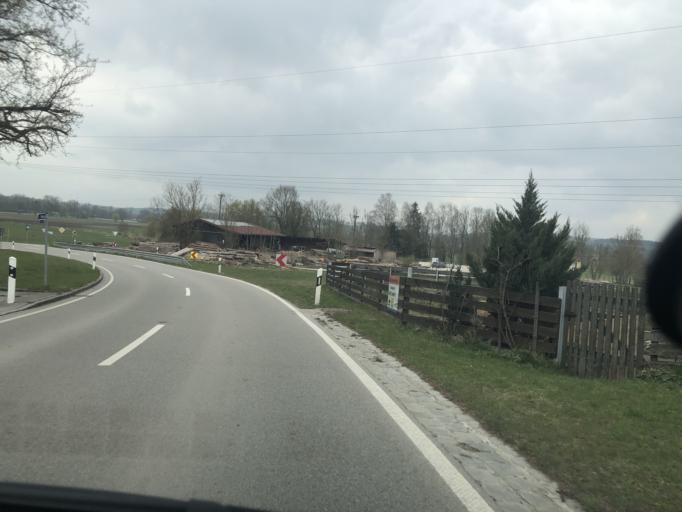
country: DE
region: Bavaria
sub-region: Upper Bavaria
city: Kirchdorf
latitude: 48.4452
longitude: 11.6706
